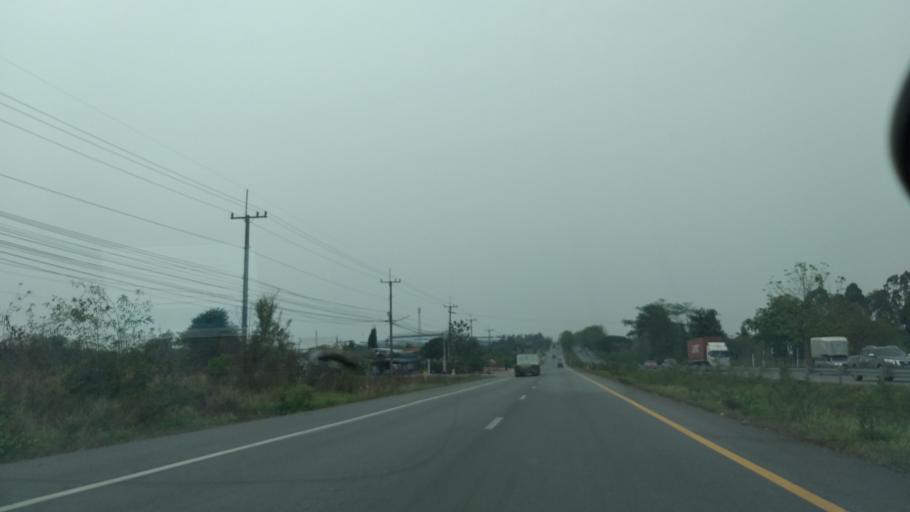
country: TH
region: Chachoengsao
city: Plaeng Yao
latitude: 13.4976
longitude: 101.2722
